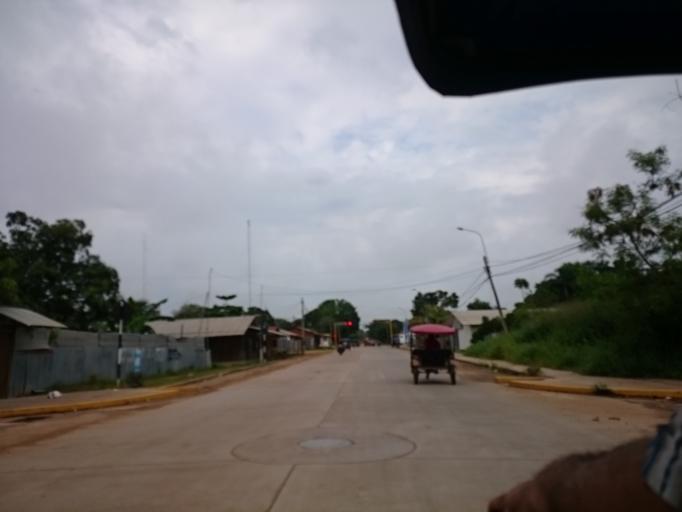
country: PE
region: Ucayali
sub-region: Provincia de Coronel Portillo
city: Puerto Callao
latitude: -8.3660
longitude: -74.5740
